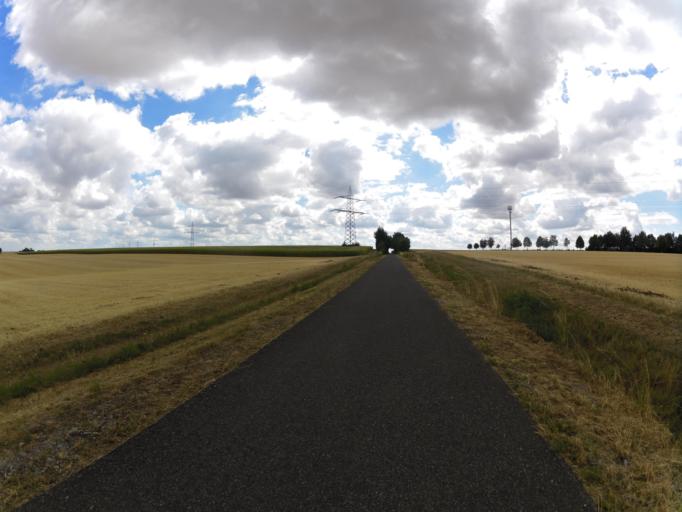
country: DE
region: Bavaria
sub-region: Regierungsbezirk Unterfranken
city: Sonderhofen
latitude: 49.5868
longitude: 10.0082
